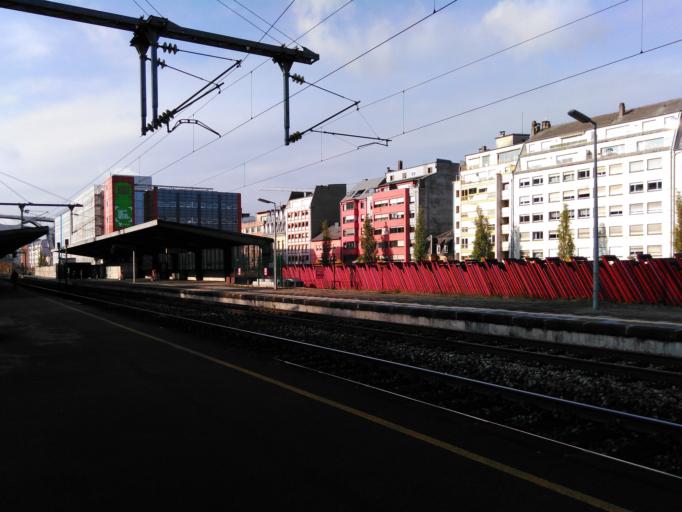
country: LU
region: Luxembourg
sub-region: Canton d'Esch-sur-Alzette
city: Esch-sur-Alzette
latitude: 49.4947
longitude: 5.9867
